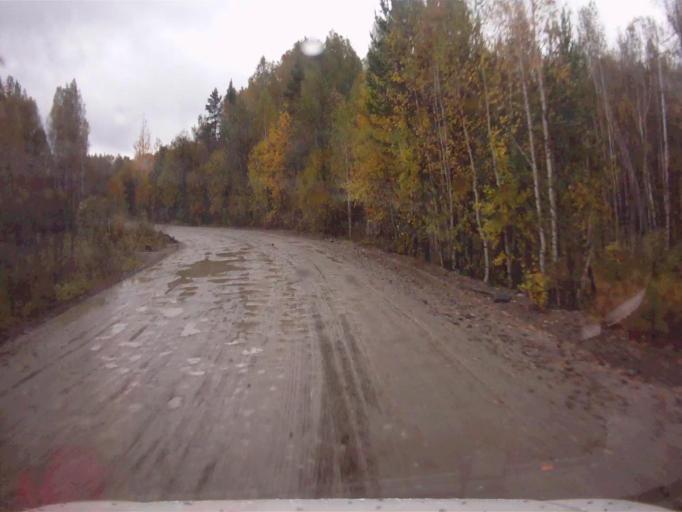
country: RU
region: Chelyabinsk
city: Kyshtym
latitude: 55.8256
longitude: 60.4857
